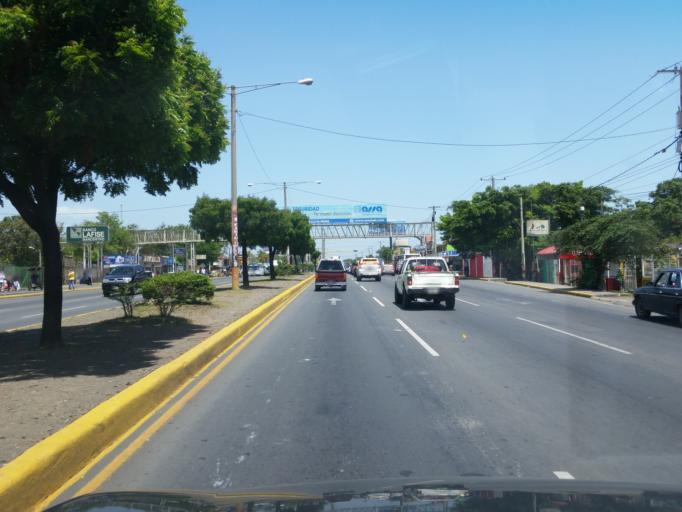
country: NI
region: Managua
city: Managua
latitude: 12.1477
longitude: -86.1924
